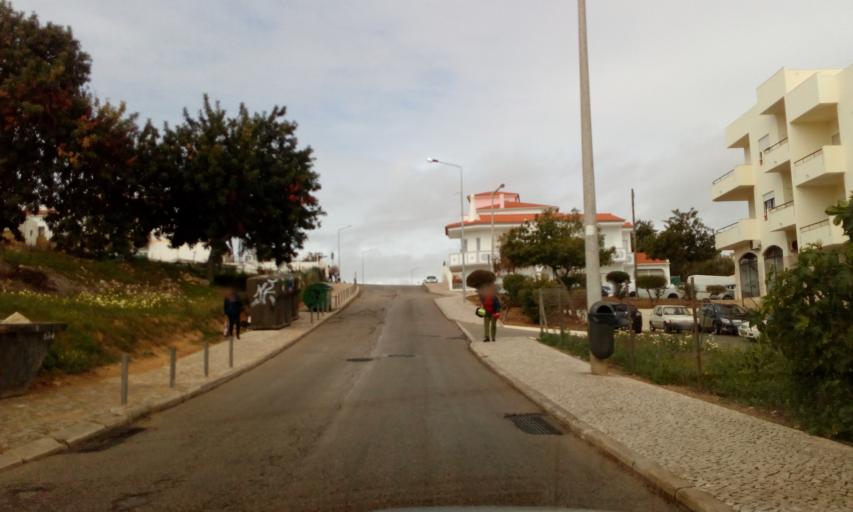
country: PT
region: Faro
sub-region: Albufeira
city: Albufeira
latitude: 37.0925
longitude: -8.2494
